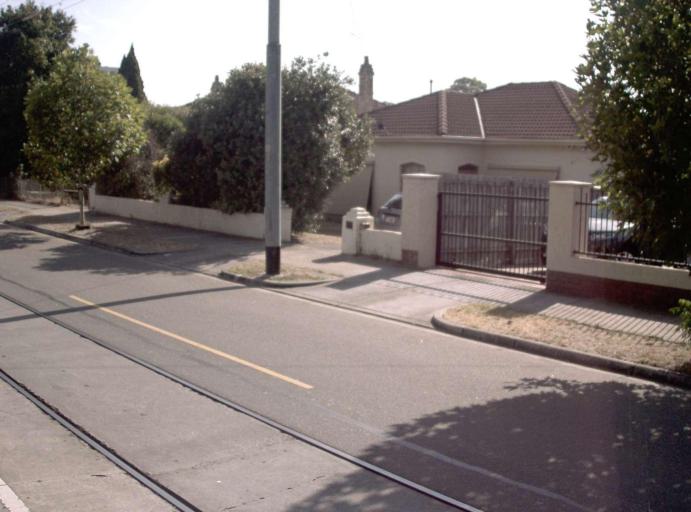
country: AU
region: Victoria
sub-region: Glen Eira
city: Caulfield South
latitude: -37.8911
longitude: 145.0212
